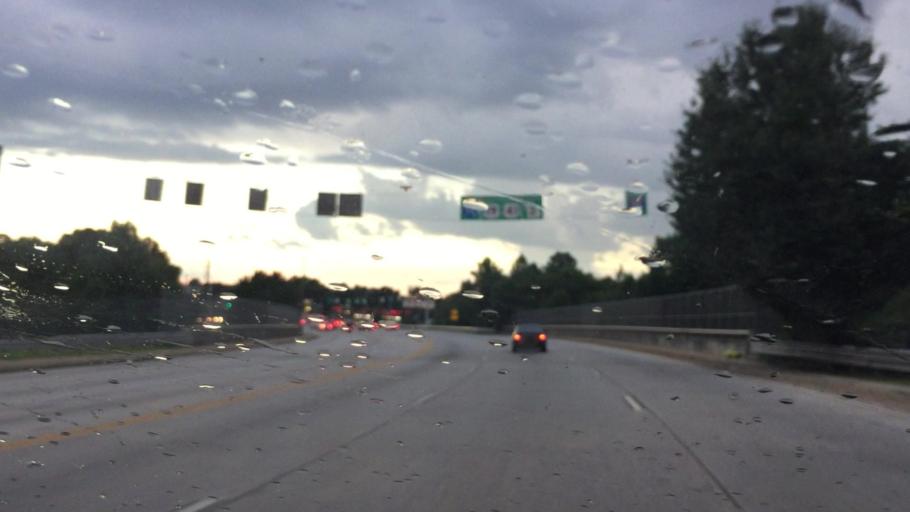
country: US
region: Georgia
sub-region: Clayton County
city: Forest Park
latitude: 33.5862
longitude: -84.3784
